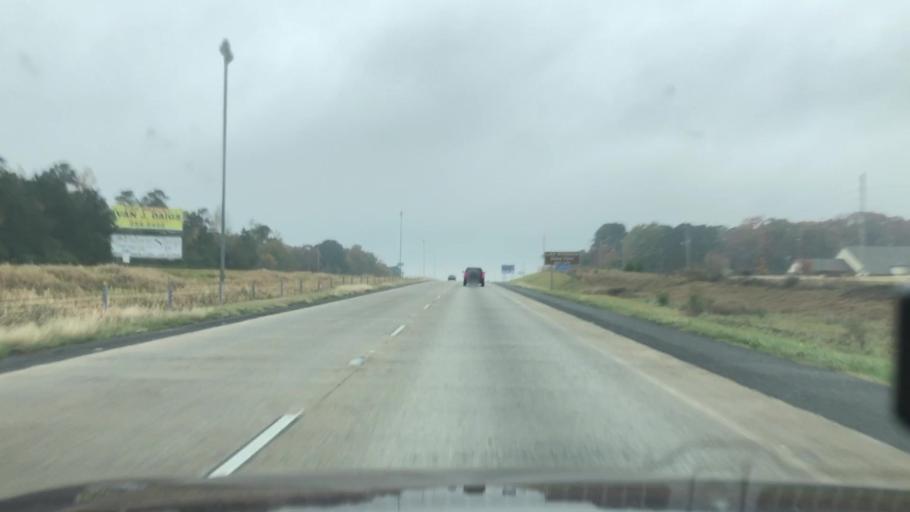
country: US
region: Louisiana
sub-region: Lincoln Parish
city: Ruston
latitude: 32.5406
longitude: -92.6059
